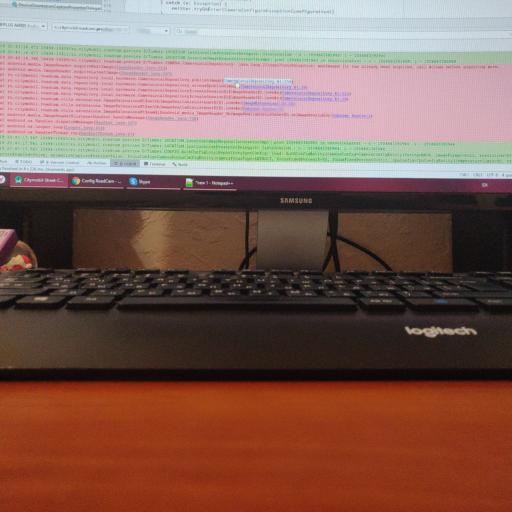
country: PL
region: Masovian Voivodeship
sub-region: Powiat plonski
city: Dzierzaznia
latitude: 52.5966
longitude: 20.2487
